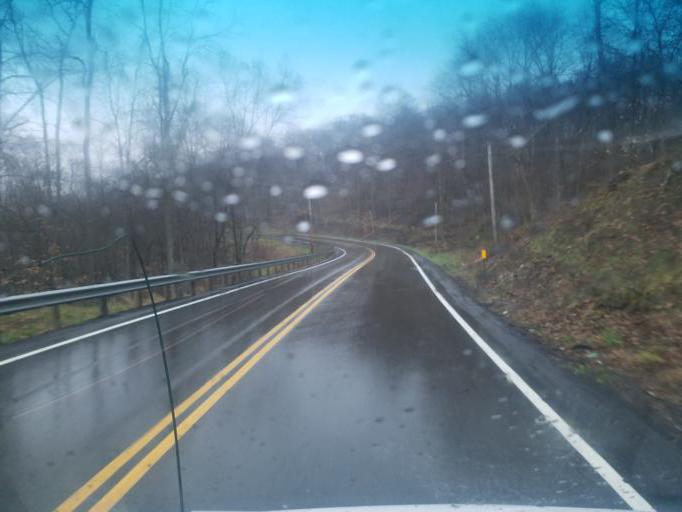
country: US
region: Ohio
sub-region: Knox County
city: Oak Hill
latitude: 40.4632
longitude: -82.1183
